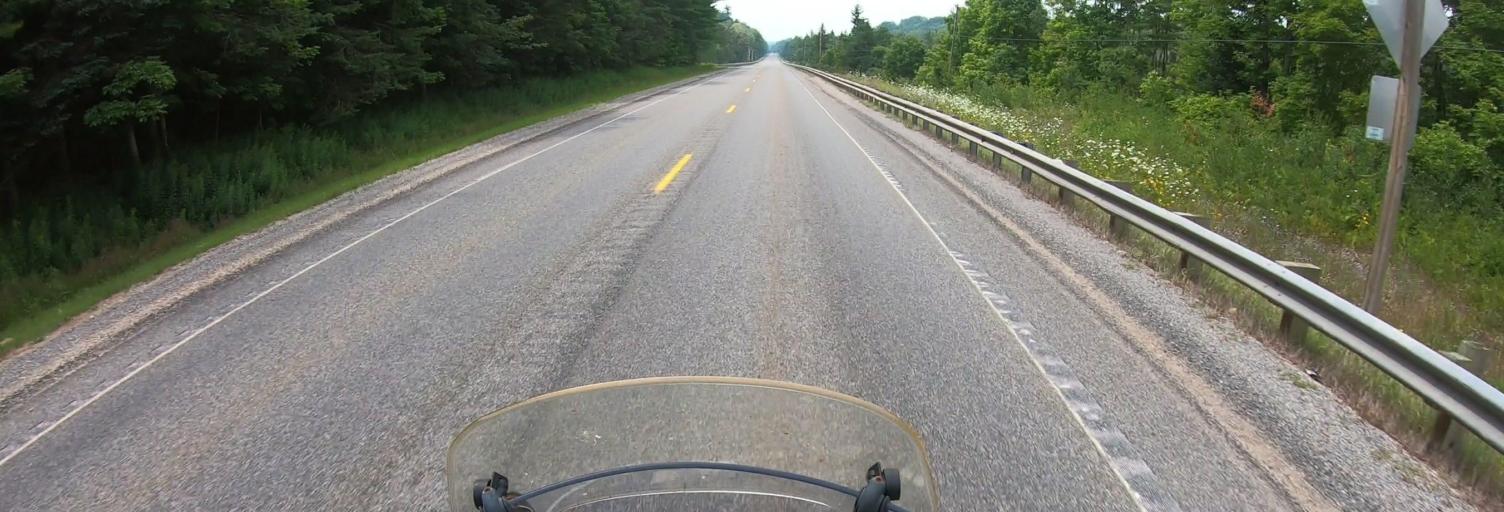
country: US
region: Michigan
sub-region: Alger County
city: Munising
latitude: 46.3879
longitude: -86.6539
